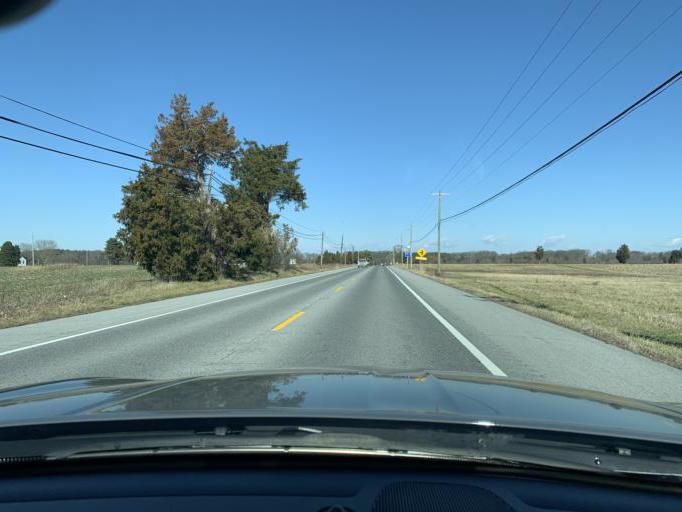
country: US
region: Maryland
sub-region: Queen Anne's County
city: Centreville
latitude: 39.0651
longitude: -76.0508
